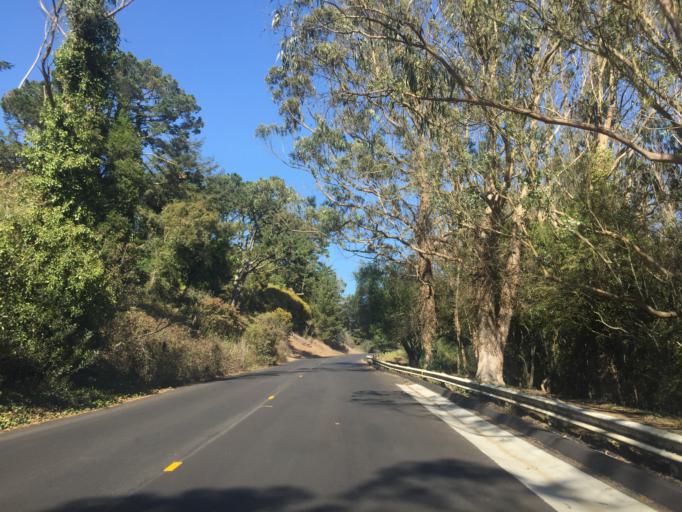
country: US
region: California
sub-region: San Francisco County
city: San Francisco
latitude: 37.7472
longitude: -122.4490
